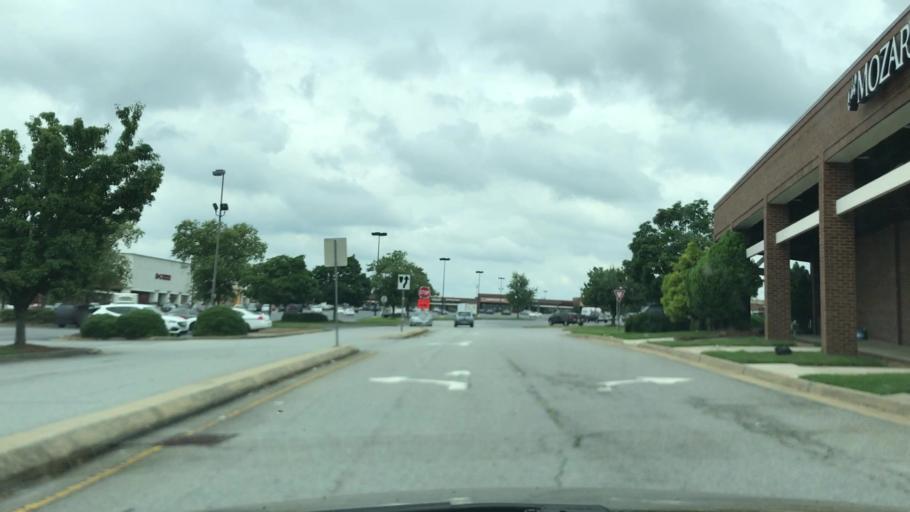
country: US
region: Georgia
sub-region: Gwinnett County
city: Duluth
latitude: 33.9543
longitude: -84.1327
